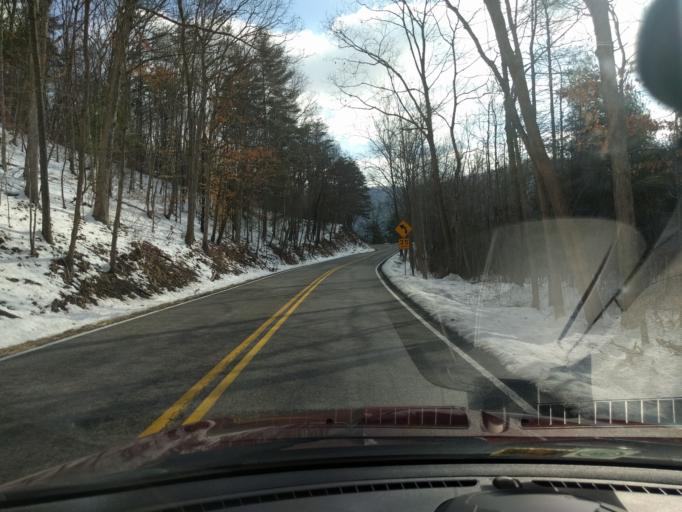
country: US
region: Virginia
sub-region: Bath County
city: Warm Springs
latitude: 38.1070
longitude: -79.9022
